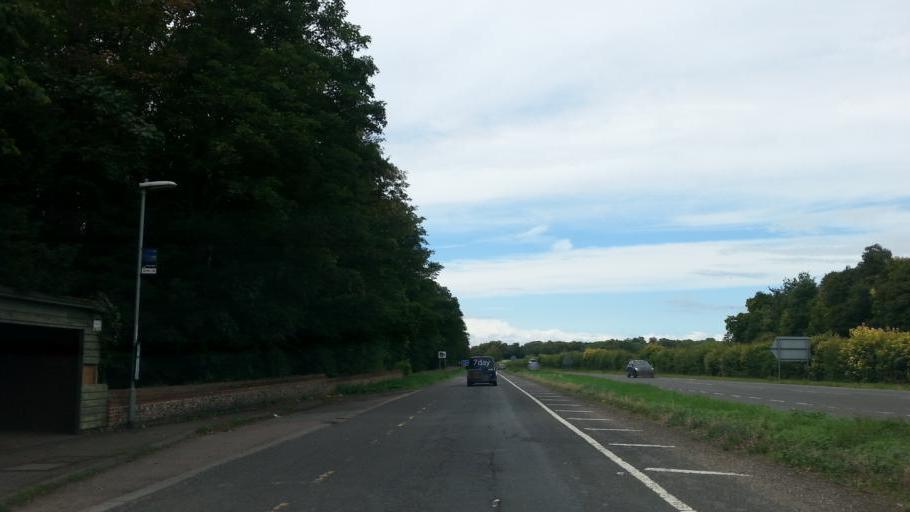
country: GB
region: England
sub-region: Cambridgeshire
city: Sawston
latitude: 52.1337
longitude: 0.2136
